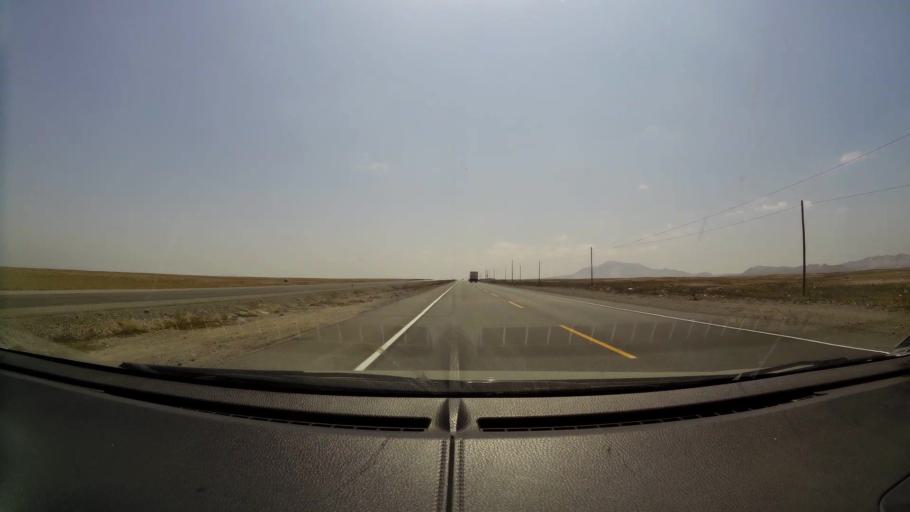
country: PE
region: Lambayeque
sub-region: Provincia de Chiclayo
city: Mocupe
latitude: -6.9502
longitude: -79.7050
